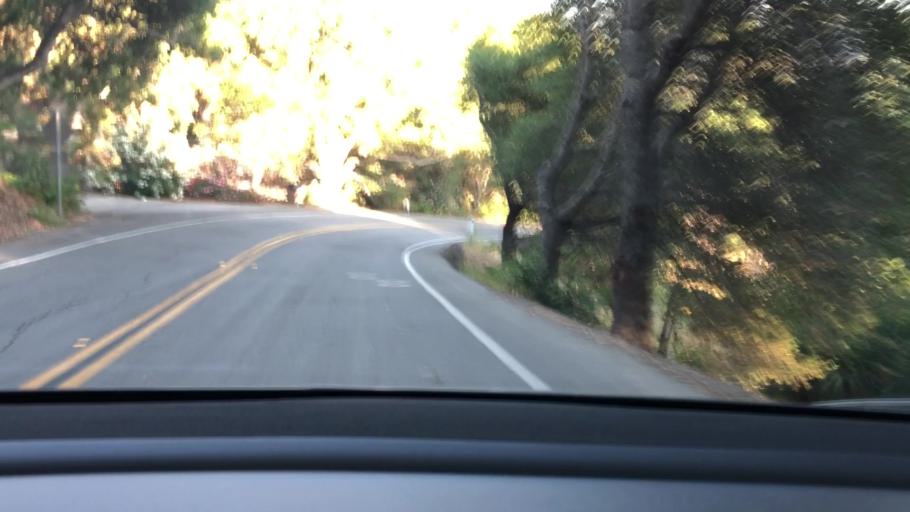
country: US
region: California
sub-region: Santa Clara County
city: Saratoga
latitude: 37.2709
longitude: -122.0607
